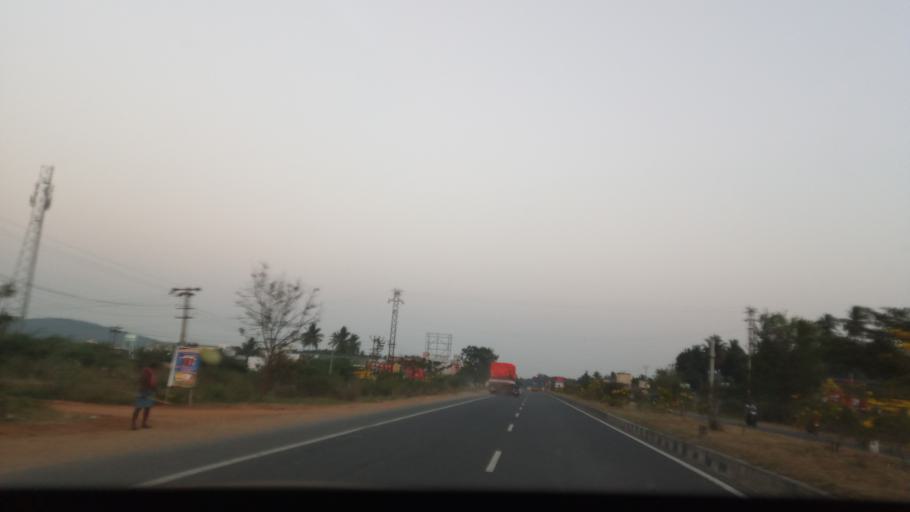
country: IN
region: Tamil Nadu
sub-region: Salem
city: Belur
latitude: 11.6594
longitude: 78.3339
